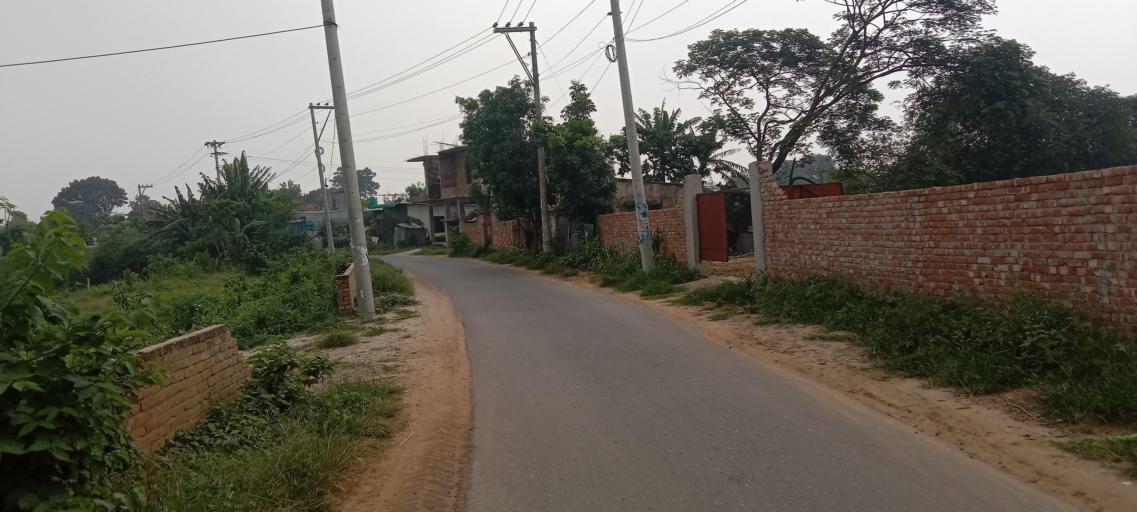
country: BD
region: Dhaka
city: Azimpur
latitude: 23.7380
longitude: 90.3186
